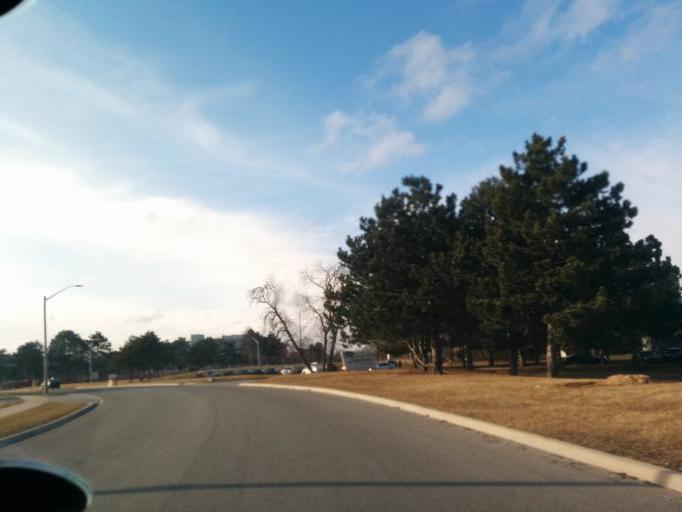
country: CA
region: Ontario
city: Mississauga
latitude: 43.5223
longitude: -79.6557
